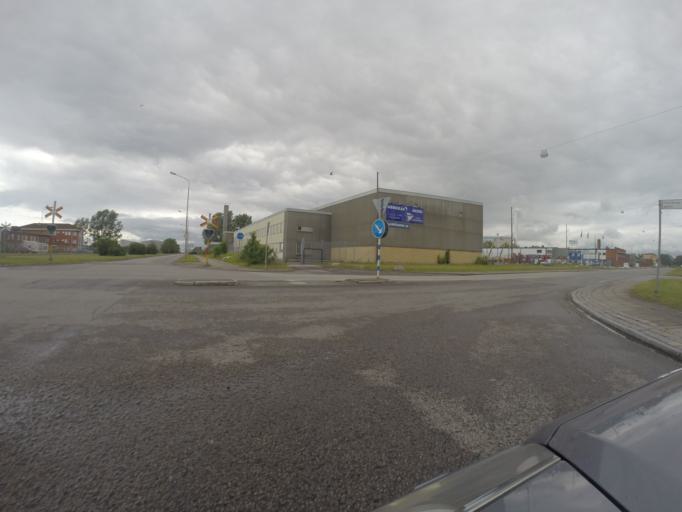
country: SE
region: Skane
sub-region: Burlovs Kommun
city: Arloev
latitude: 55.6280
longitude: 13.0369
